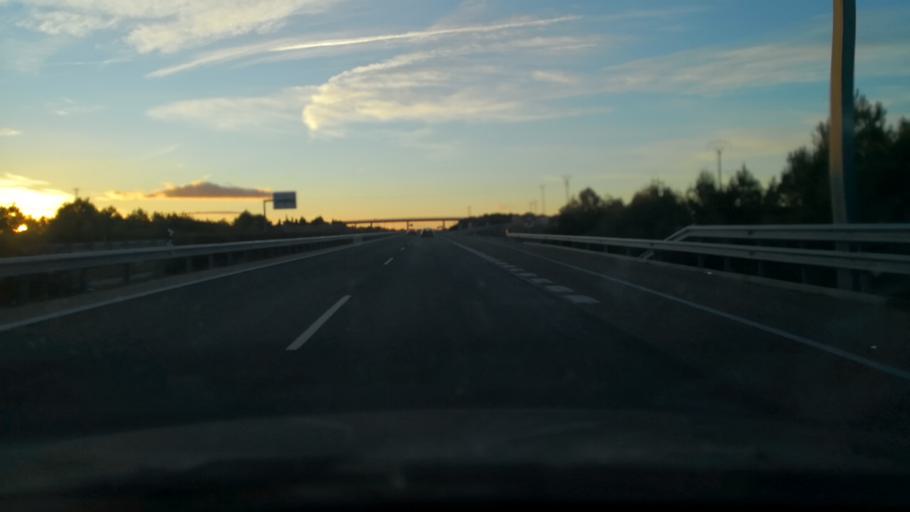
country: ES
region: Castille and Leon
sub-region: Provincia de Valladolid
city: Tordesillas
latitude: 41.5045
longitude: -5.0376
